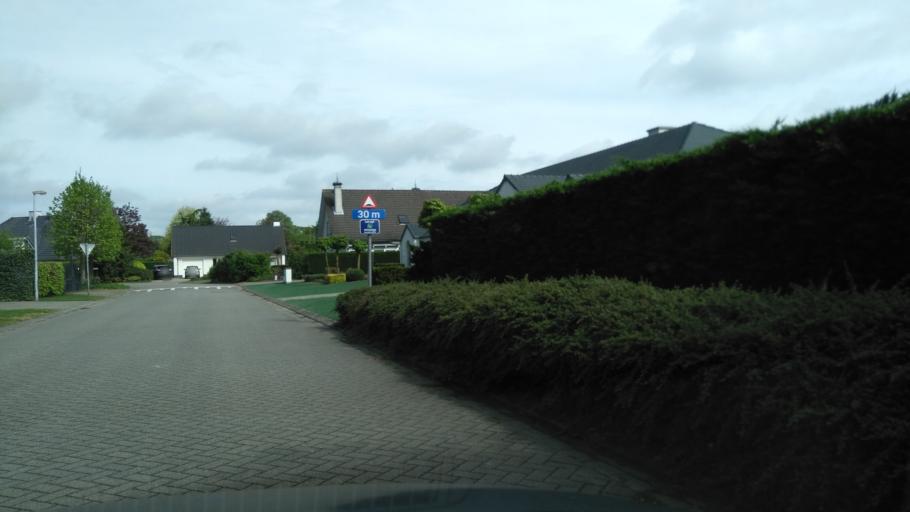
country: BE
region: Flanders
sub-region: Provincie Antwerpen
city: Baarle-Hertog
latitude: 51.3937
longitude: 4.9416
